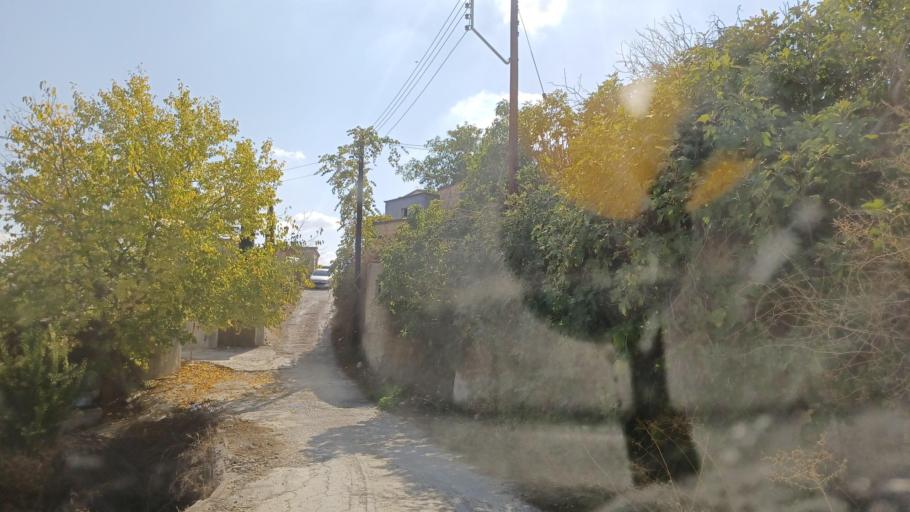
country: CY
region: Pafos
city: Tala
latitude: 34.9128
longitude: 32.4553
